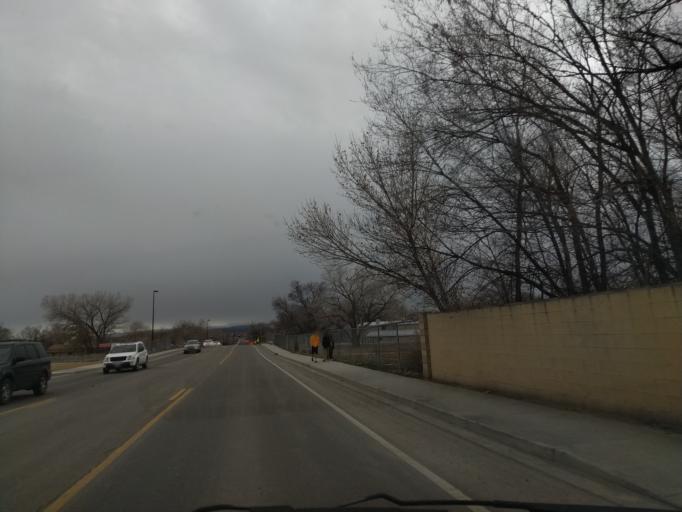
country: US
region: Colorado
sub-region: Mesa County
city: Fruitvale
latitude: 39.0872
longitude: -108.5152
